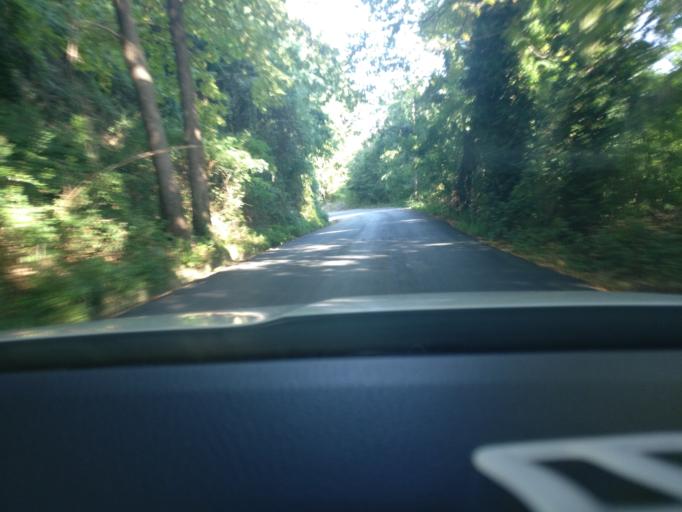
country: GR
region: Thessaly
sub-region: Nomos Magnisias
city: Zagora
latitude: 39.3837
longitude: 23.1798
